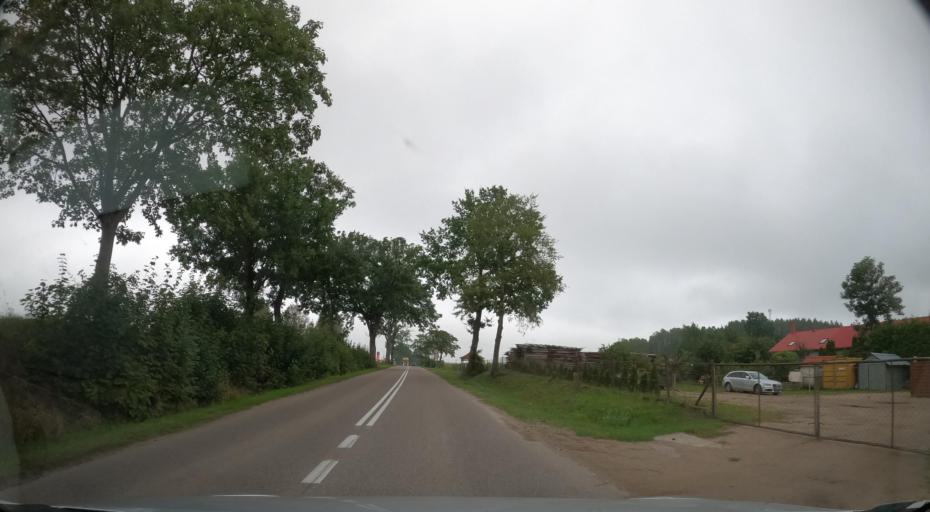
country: PL
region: Pomeranian Voivodeship
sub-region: Powiat wejherowski
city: Linia
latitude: 54.4561
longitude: 18.0360
